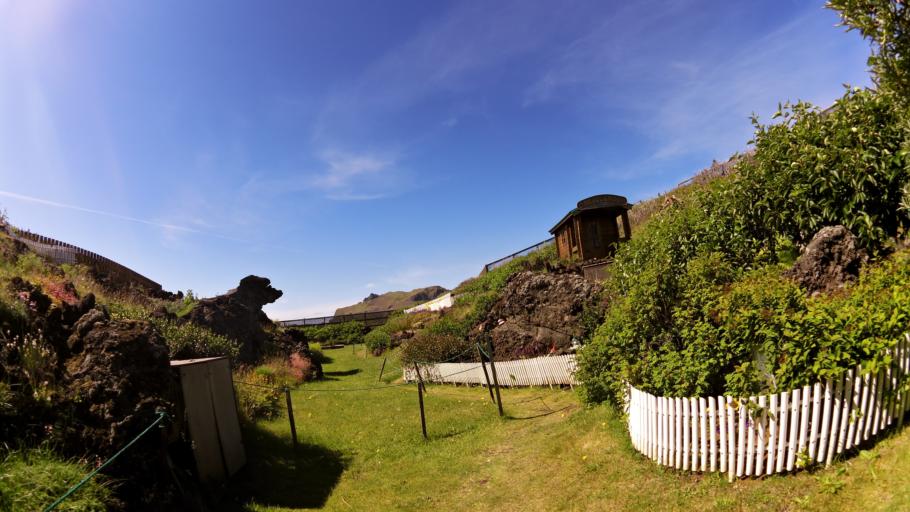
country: IS
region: South
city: Vestmannaeyjar
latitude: 63.4429
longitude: -20.2486
